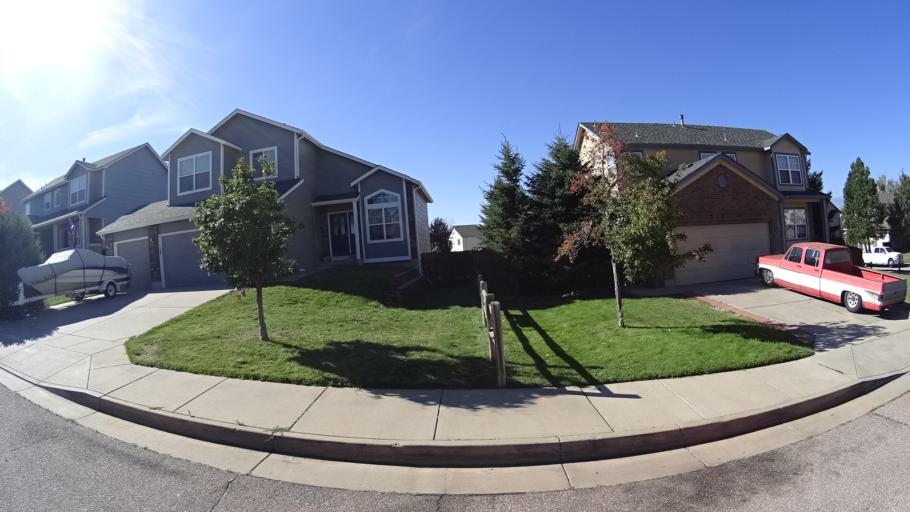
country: US
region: Colorado
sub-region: El Paso County
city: Black Forest
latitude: 38.9465
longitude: -104.7372
